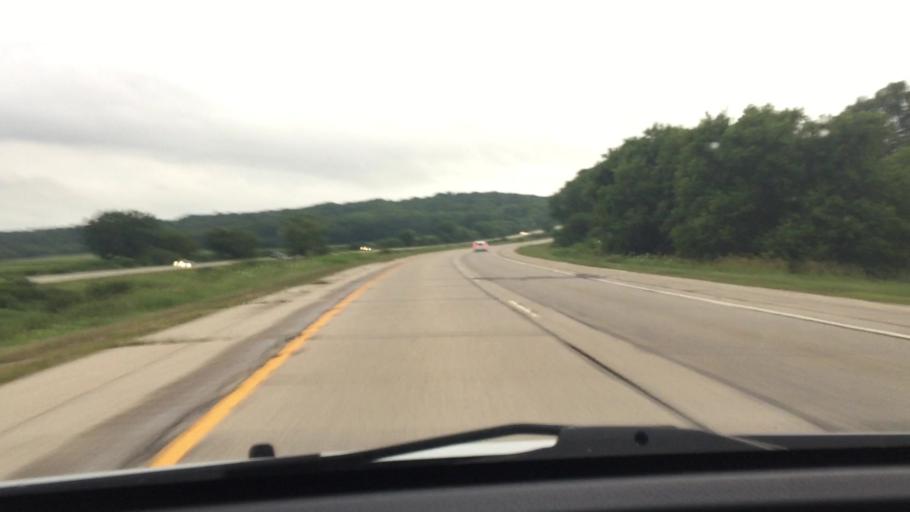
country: US
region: Wisconsin
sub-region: Walworth County
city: Como
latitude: 42.6171
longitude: -88.4559
